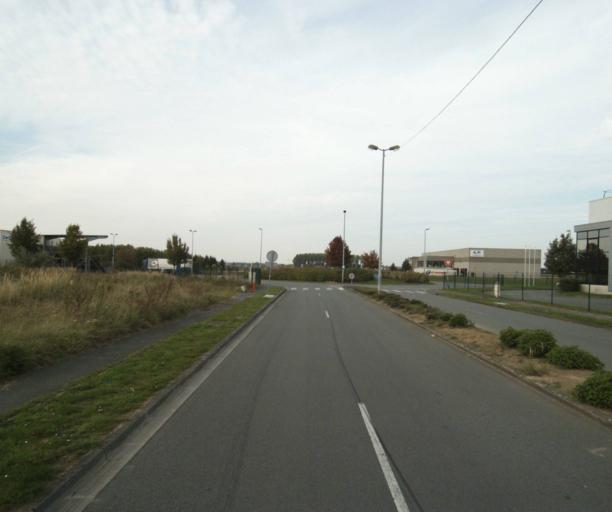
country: FR
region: Nord-Pas-de-Calais
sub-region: Departement du Nord
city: Templemars
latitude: 50.5575
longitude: 3.0586
